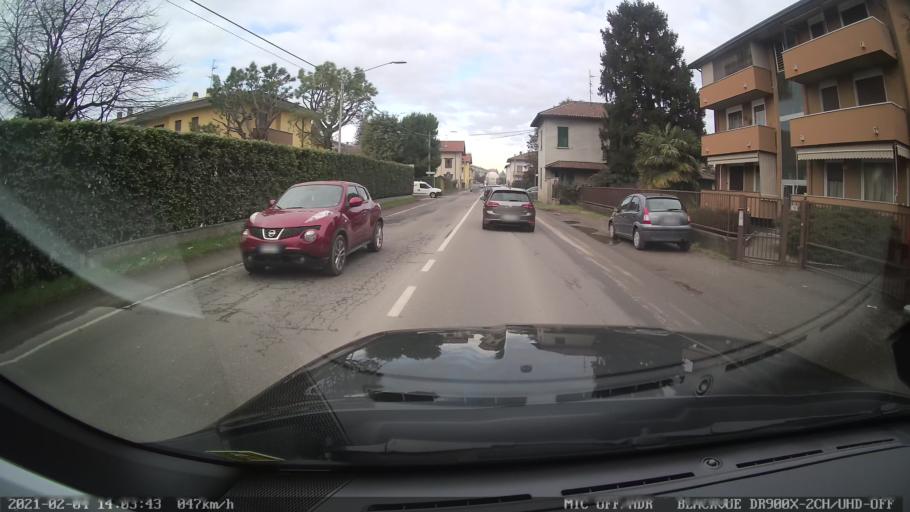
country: IT
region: Lombardy
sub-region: Provincia di Varese
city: Tradate
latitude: 45.7150
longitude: 8.8983
